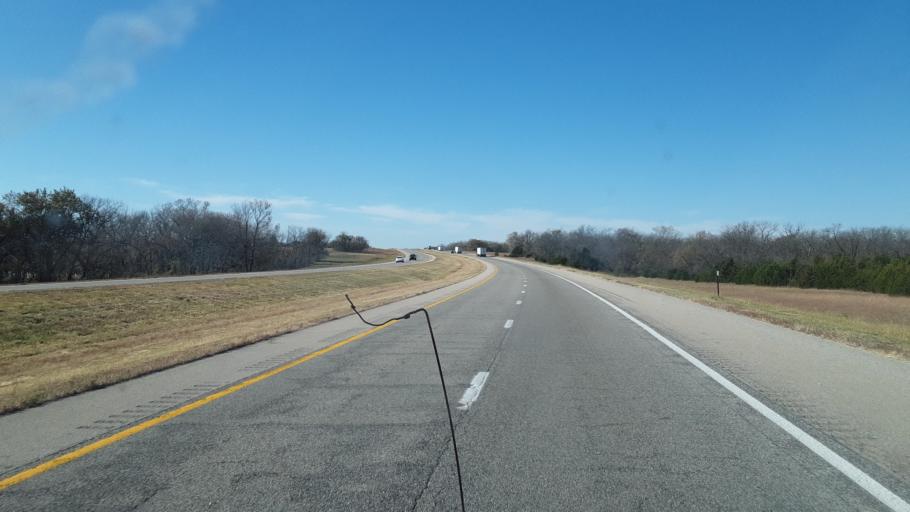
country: US
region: Kansas
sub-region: Osage County
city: Osage City
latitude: 38.4282
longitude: -95.8851
